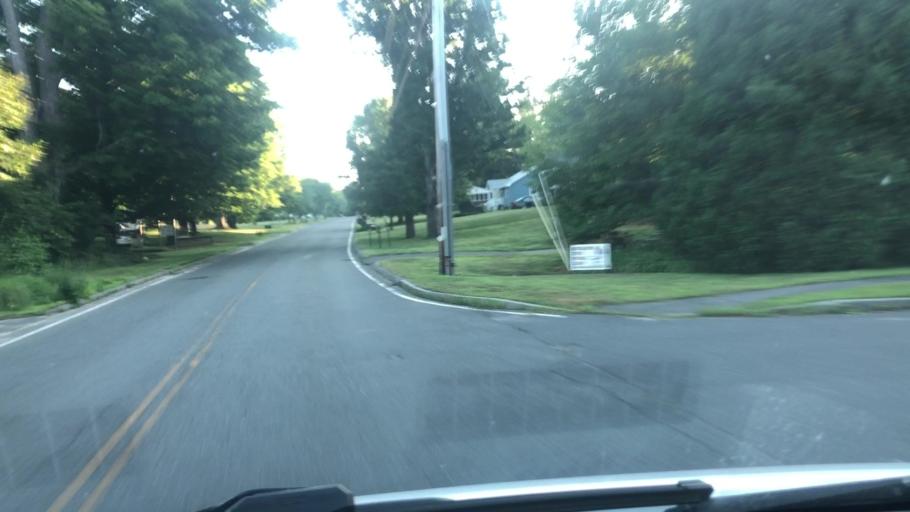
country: US
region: Massachusetts
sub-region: Hampshire County
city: Westhampton
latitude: 42.3000
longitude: -72.7167
